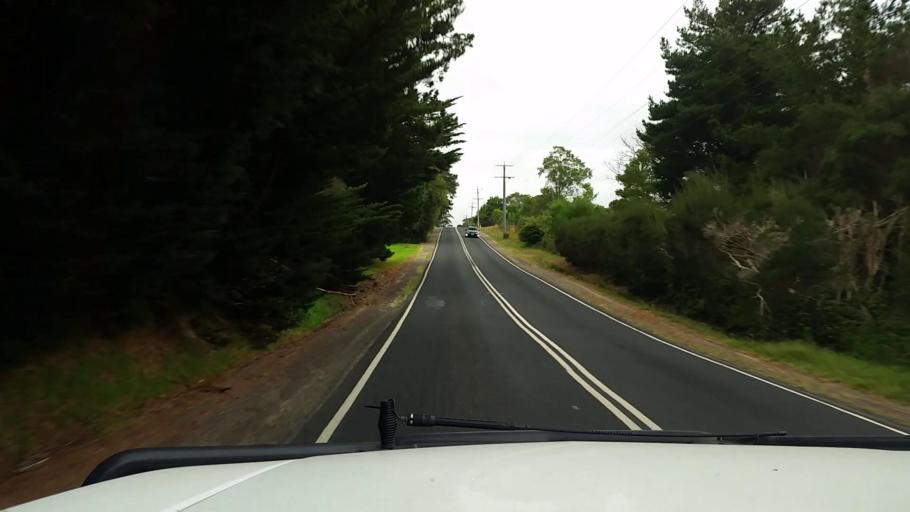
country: AU
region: Victoria
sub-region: Mornington Peninsula
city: Hastings
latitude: -38.2930
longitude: 145.1456
